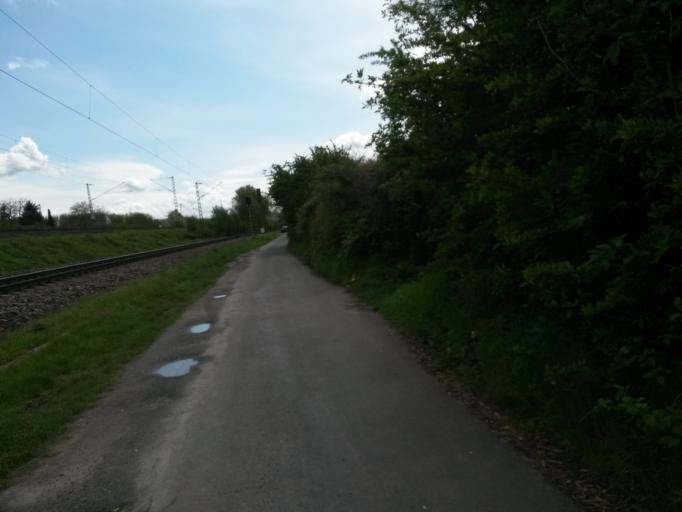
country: DE
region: Baden-Wuerttemberg
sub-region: Karlsruhe Region
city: Karlsruhe
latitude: 49.0179
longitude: 8.4512
